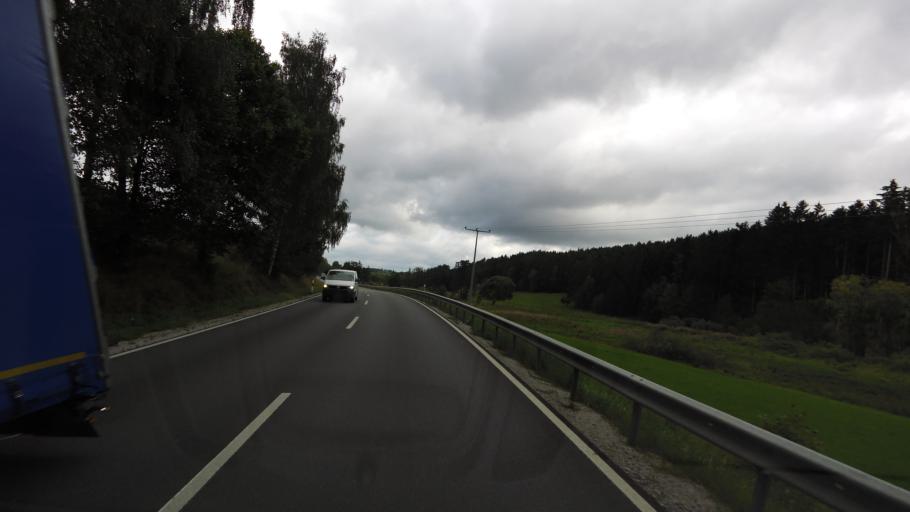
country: DE
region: Bavaria
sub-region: Upper Palatinate
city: Traitsching
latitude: 49.1414
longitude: 12.6507
